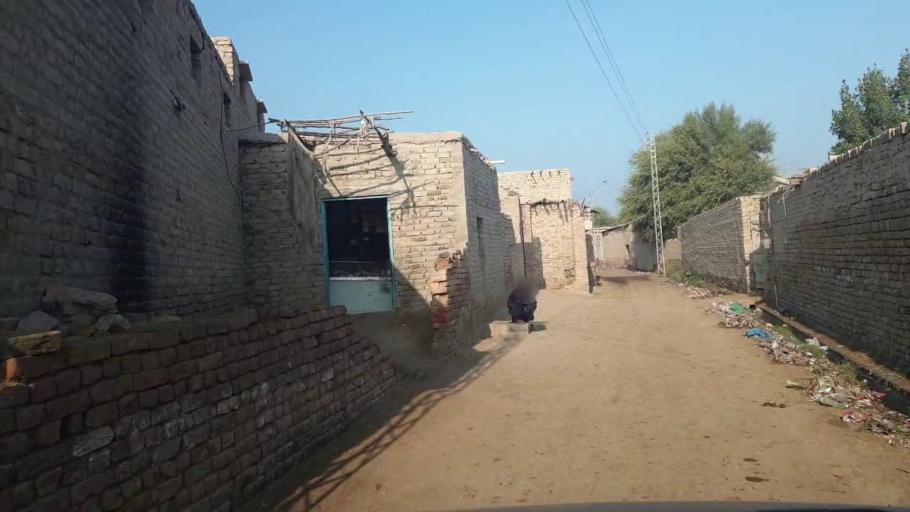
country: PK
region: Sindh
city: Shahdadpur
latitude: 25.9434
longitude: 68.6063
